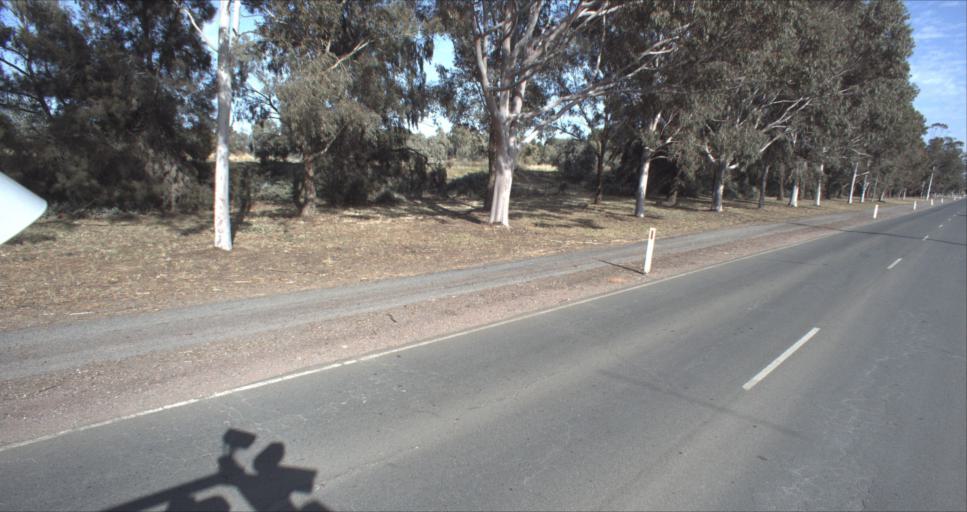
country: AU
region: New South Wales
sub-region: Leeton
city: Leeton
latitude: -34.5556
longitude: 146.3885
